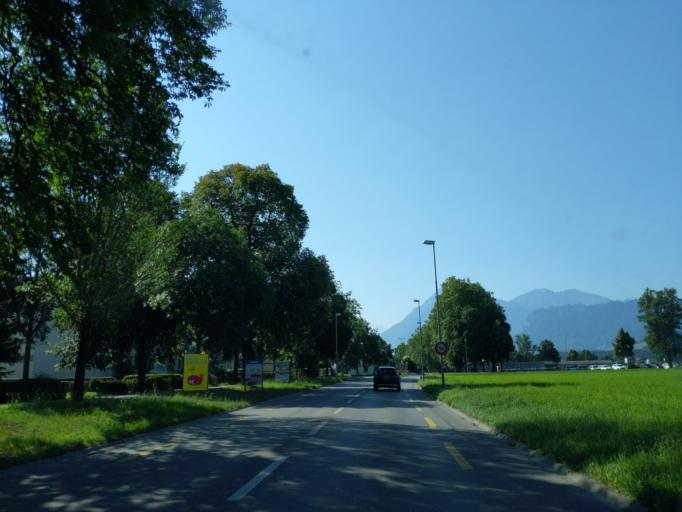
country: CH
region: Bern
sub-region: Thun District
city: Thun
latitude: 46.7493
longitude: 7.6105
